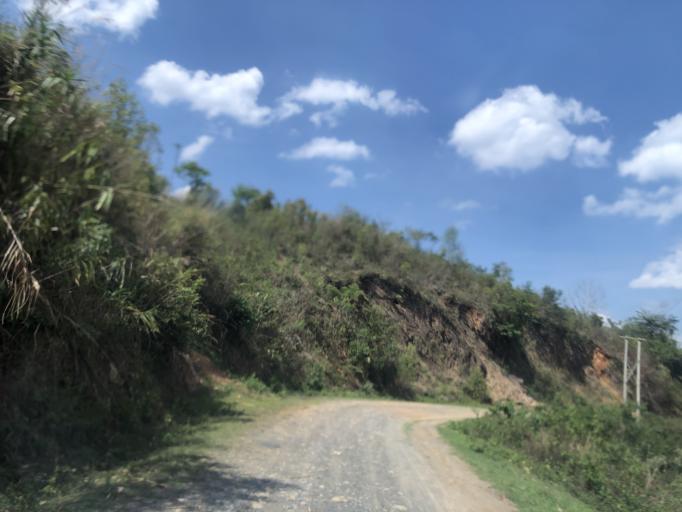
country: LA
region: Phongsali
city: Phongsali
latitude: 21.4109
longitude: 102.2403
